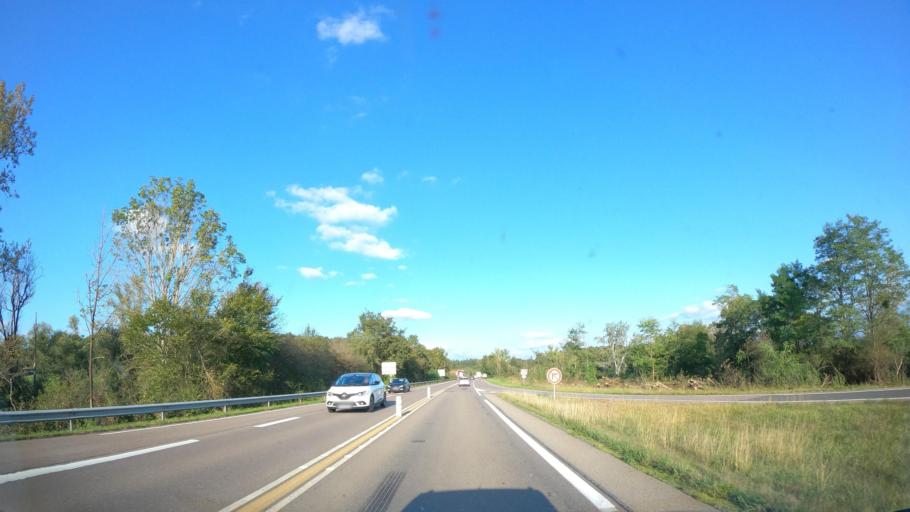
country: FR
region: Bourgogne
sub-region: Departement de Saone-et-Loire
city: Genelard
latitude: 46.6057
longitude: 4.2518
